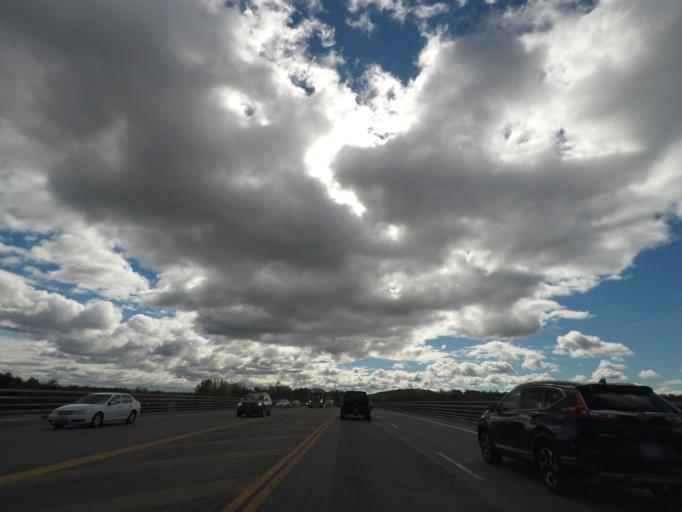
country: US
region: New York
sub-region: Albany County
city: Cohoes
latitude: 42.8217
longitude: -73.7319
